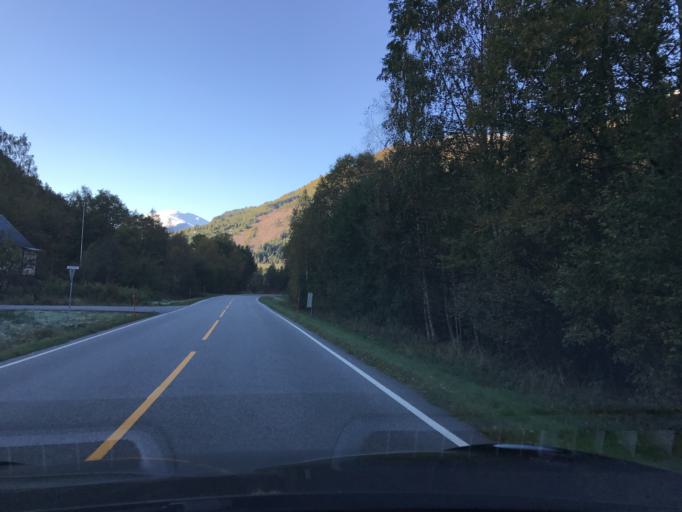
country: NO
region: More og Romsdal
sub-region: Norddal
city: Valldal
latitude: 62.3137
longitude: 7.2767
